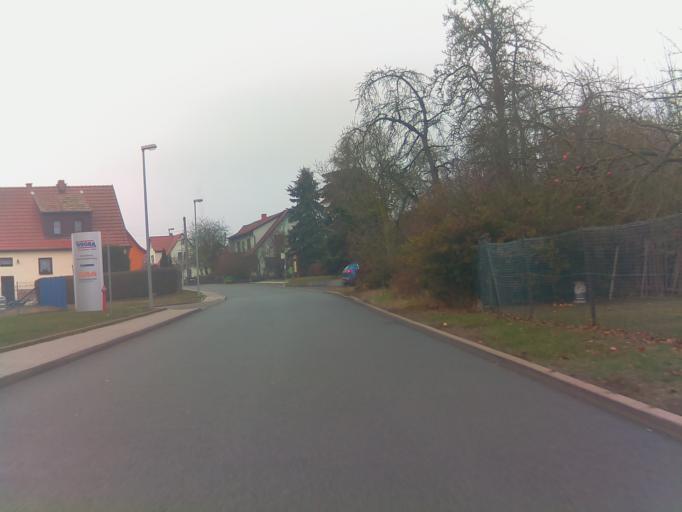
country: DE
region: Thuringia
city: Juchsen
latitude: 50.4309
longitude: 10.5015
